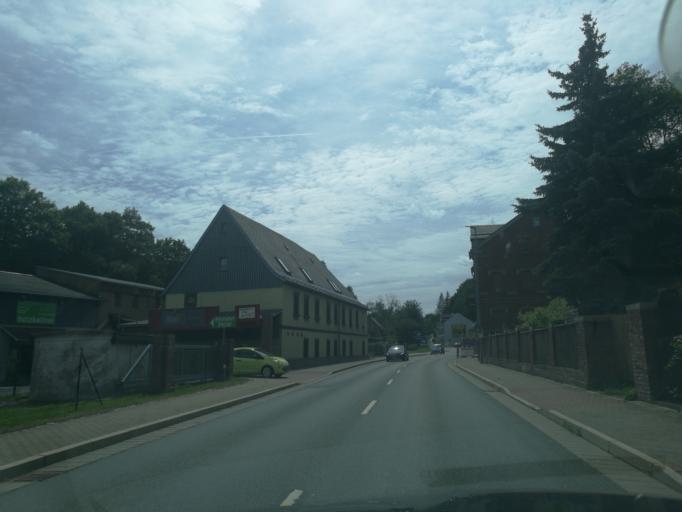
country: DE
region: Saxony
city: Adorf
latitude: 50.3235
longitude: 12.2577
